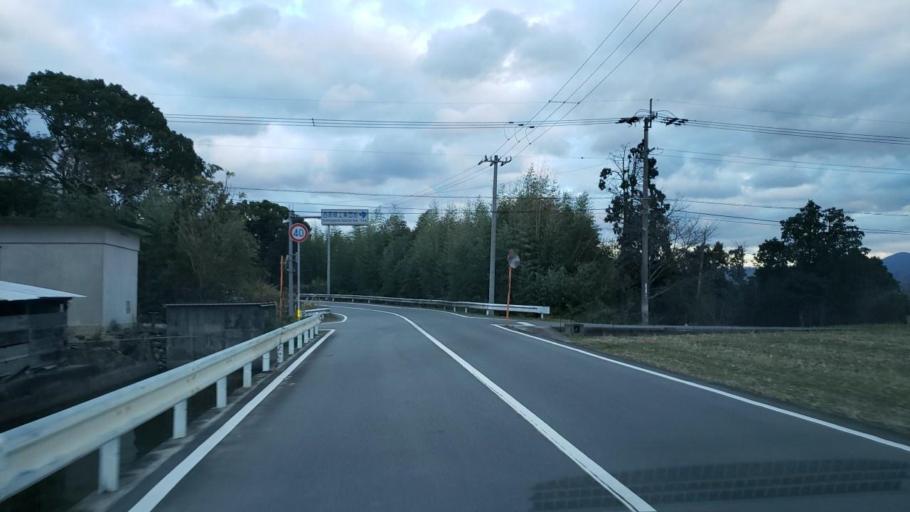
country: JP
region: Tokushima
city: Wakimachi
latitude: 34.0847
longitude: 134.1794
